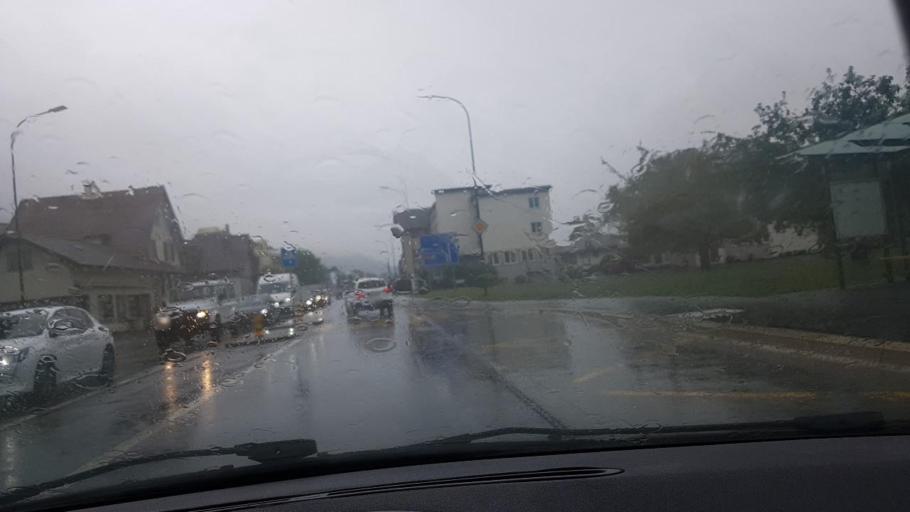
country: LI
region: Vaduz
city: Vaduz
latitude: 47.1314
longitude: 9.5224
